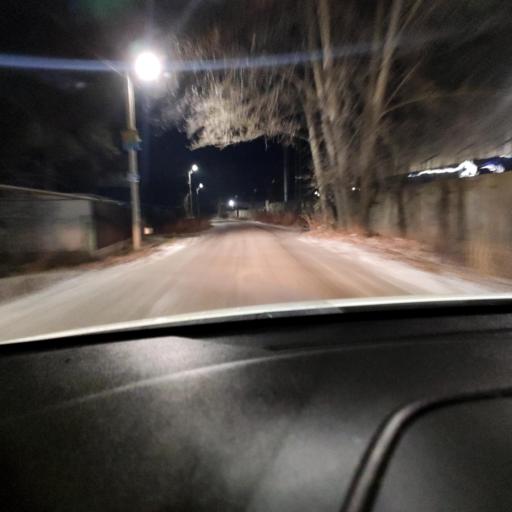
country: RU
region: Tatarstan
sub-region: Gorod Kazan'
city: Kazan
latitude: 55.7232
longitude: 49.0991
